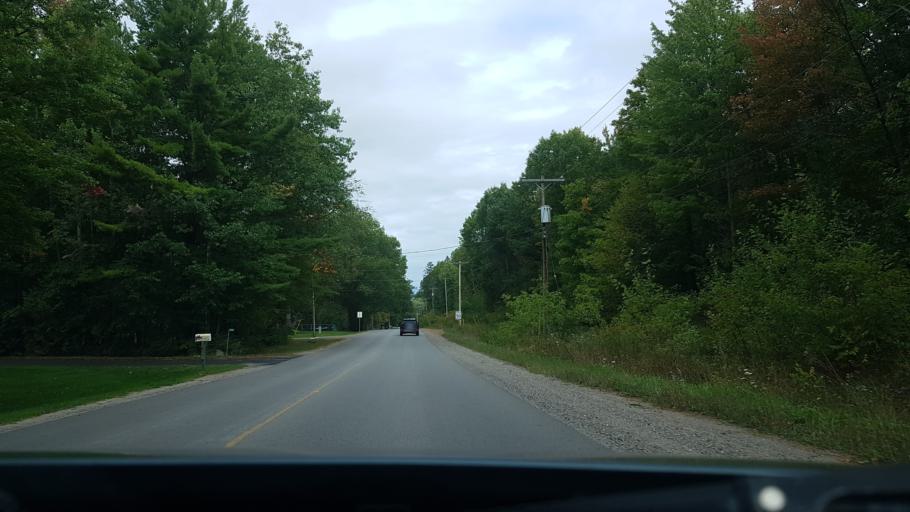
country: CA
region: Ontario
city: Barrie
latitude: 44.4836
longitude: -79.8156
